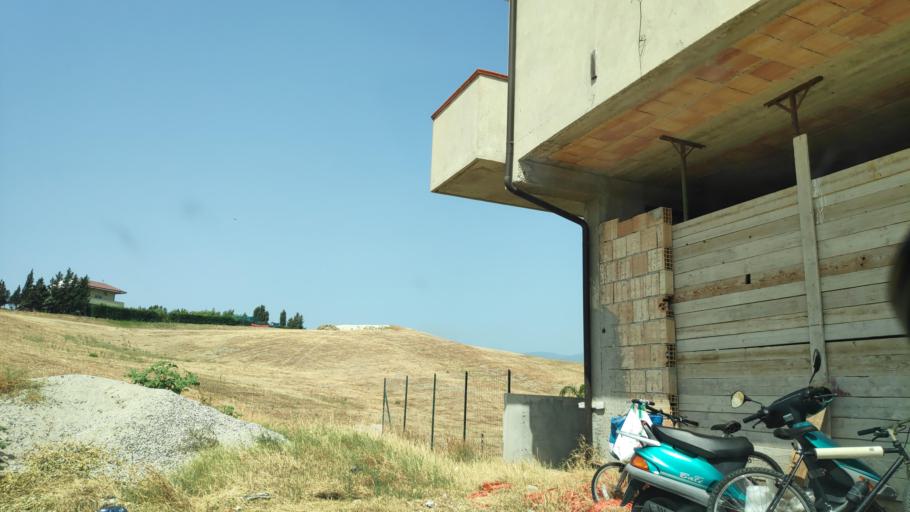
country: IT
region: Calabria
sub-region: Provincia di Catanzaro
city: Guardavalle Marina
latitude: 38.4836
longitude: 16.5754
